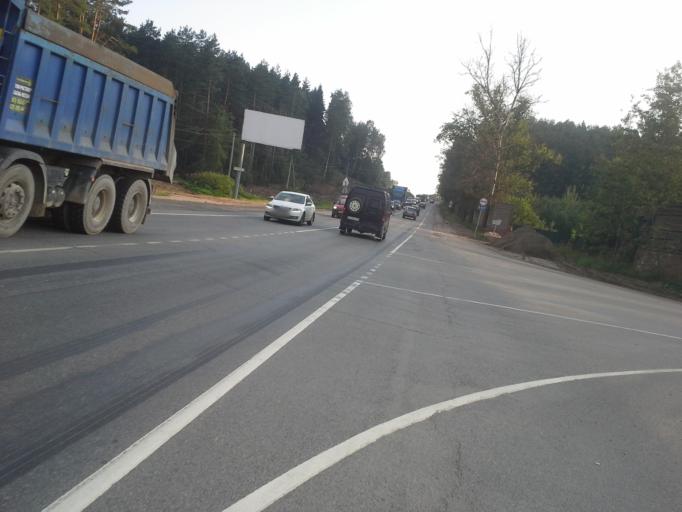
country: RU
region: Moskovskaya
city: Istra
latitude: 55.8549
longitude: 36.9316
